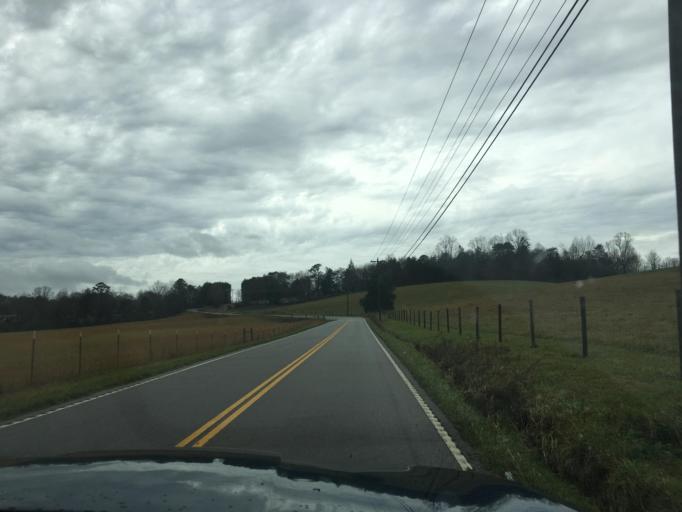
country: US
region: Tennessee
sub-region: Monroe County
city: Madisonville
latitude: 35.3721
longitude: -84.3093
